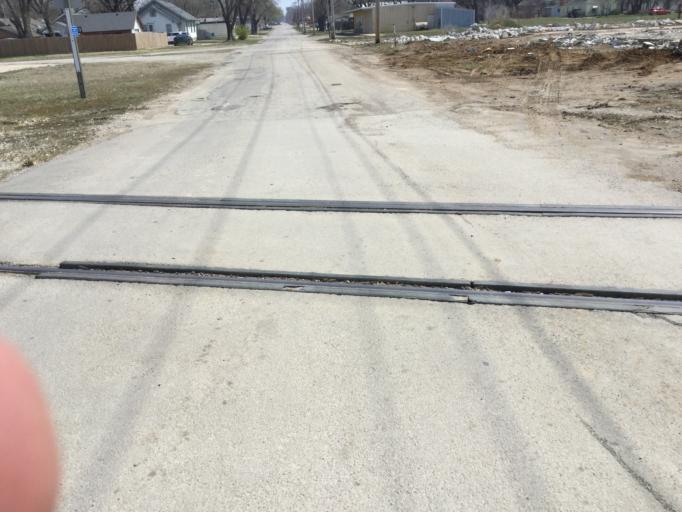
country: US
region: Kansas
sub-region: Wilson County
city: Fredonia
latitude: 37.5326
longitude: -95.8341
